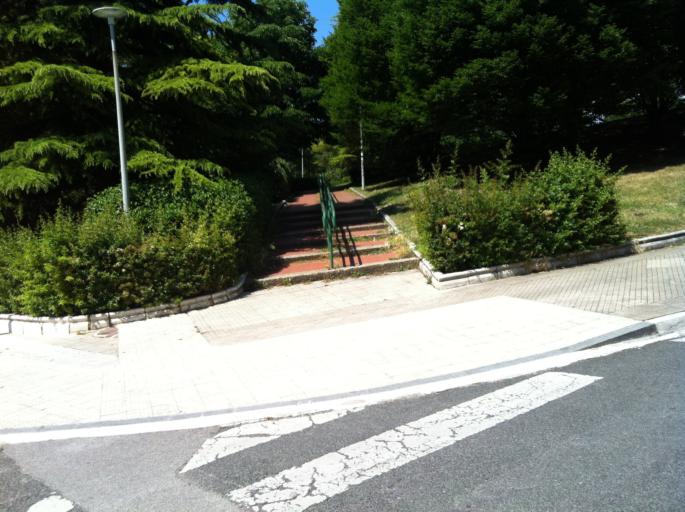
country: ES
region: Basque Country
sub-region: Provincia de Alava
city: Gasteiz / Vitoria
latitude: 42.8435
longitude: -2.6562
